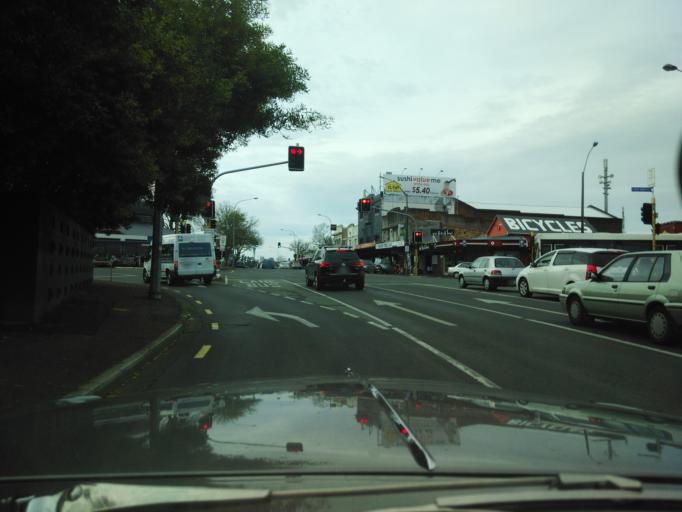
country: NZ
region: Auckland
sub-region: Auckland
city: Rosebank
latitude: -36.8710
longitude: 174.7094
